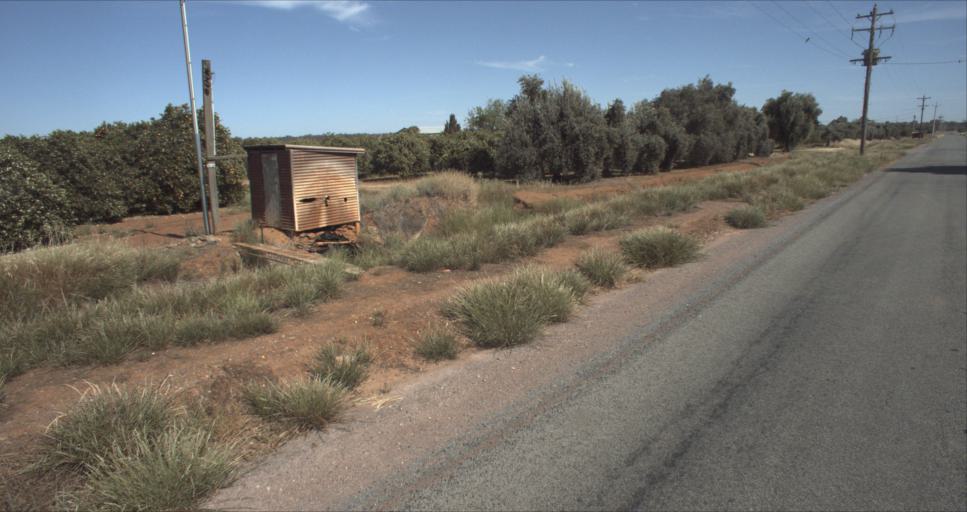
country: AU
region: New South Wales
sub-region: Leeton
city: Leeton
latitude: -34.5861
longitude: 146.4721
